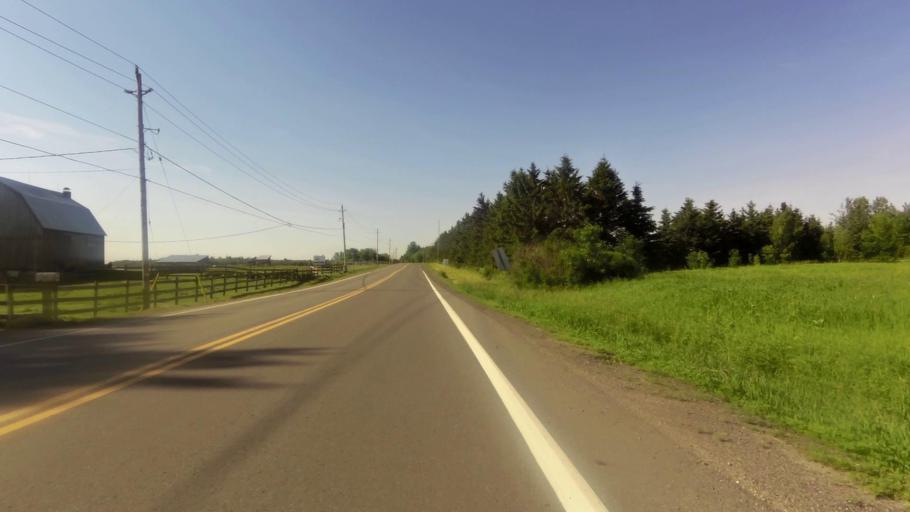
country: CA
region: Ontario
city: Ottawa
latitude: 45.2396
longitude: -75.5610
